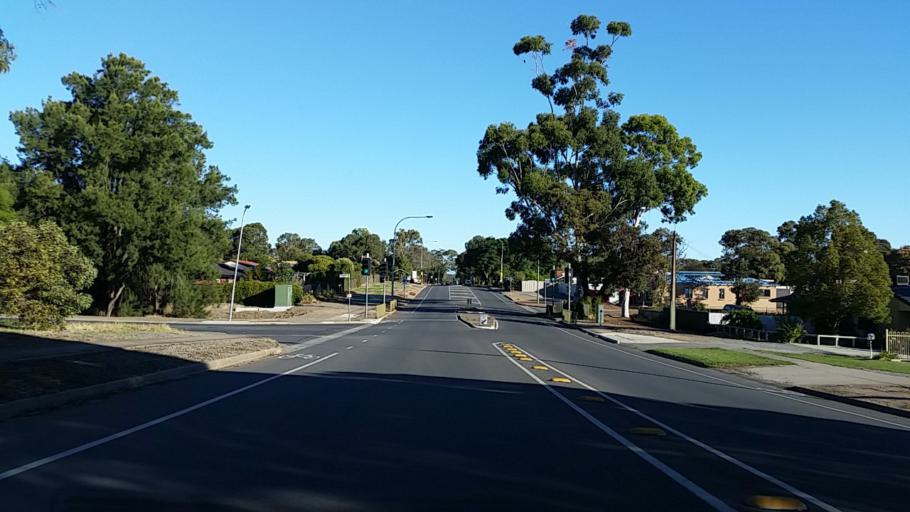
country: AU
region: South Australia
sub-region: Onkaparinga
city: Morphett Vale
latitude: -35.1188
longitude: 138.5359
